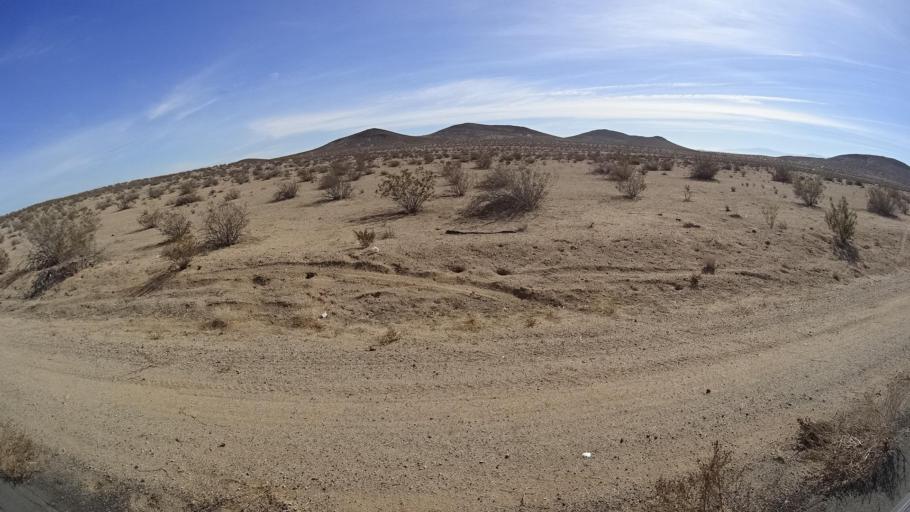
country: US
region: California
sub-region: Kern County
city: North Edwards
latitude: 35.0487
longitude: -117.8181
